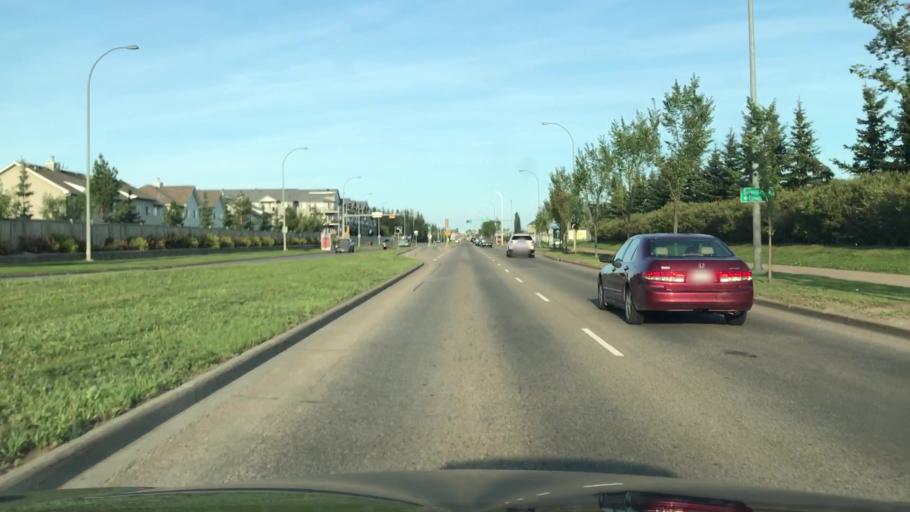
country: CA
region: Alberta
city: Beaumont
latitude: 53.4248
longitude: -113.4581
